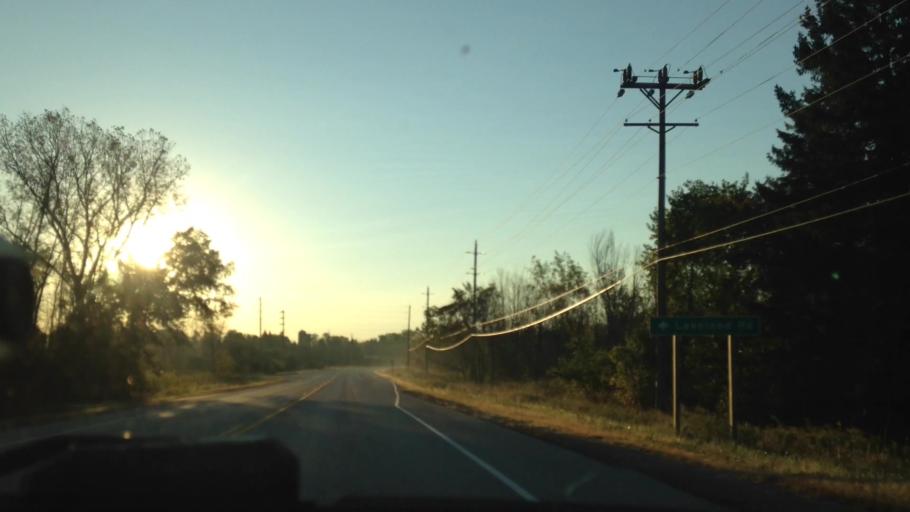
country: US
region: Wisconsin
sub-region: Washington County
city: Newburg
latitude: 43.4074
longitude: -87.9977
